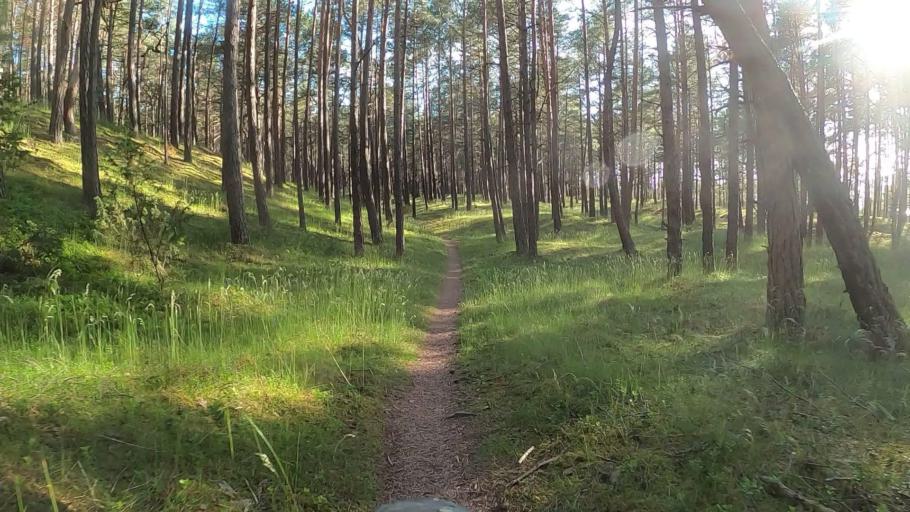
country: LV
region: Carnikava
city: Carnikava
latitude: 57.1275
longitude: 24.2192
